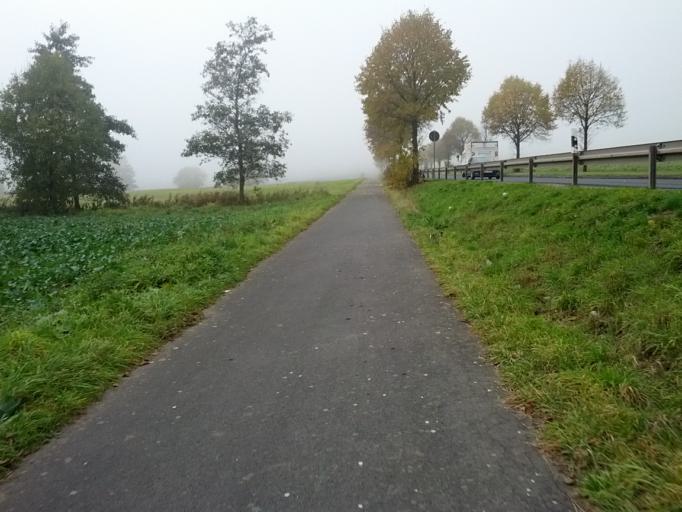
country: DE
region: Thuringia
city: Bischofroda
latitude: 50.9956
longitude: 10.3722
